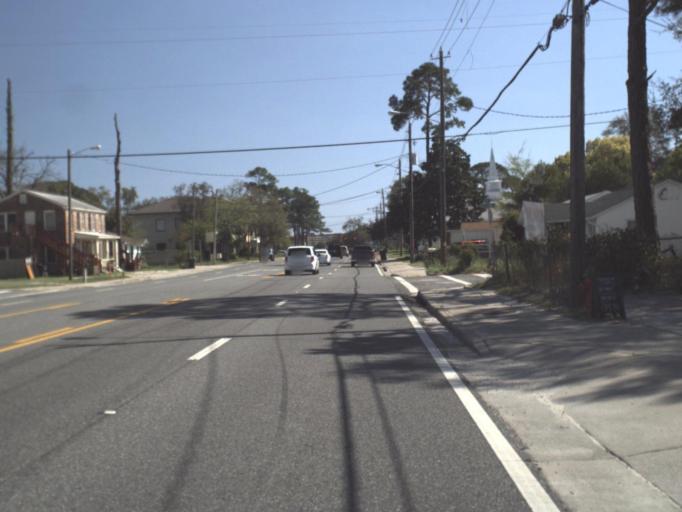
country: US
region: Florida
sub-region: Okaloosa County
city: Fort Walton Beach
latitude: 30.4075
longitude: -86.6132
